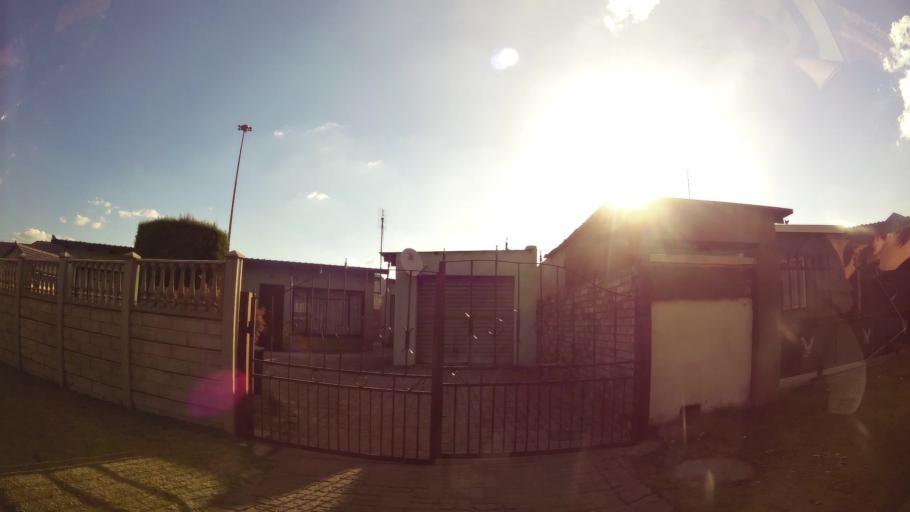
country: ZA
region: Mpumalanga
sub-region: Nkangala District Municipality
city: Witbank
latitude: -25.8700
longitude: 29.1807
